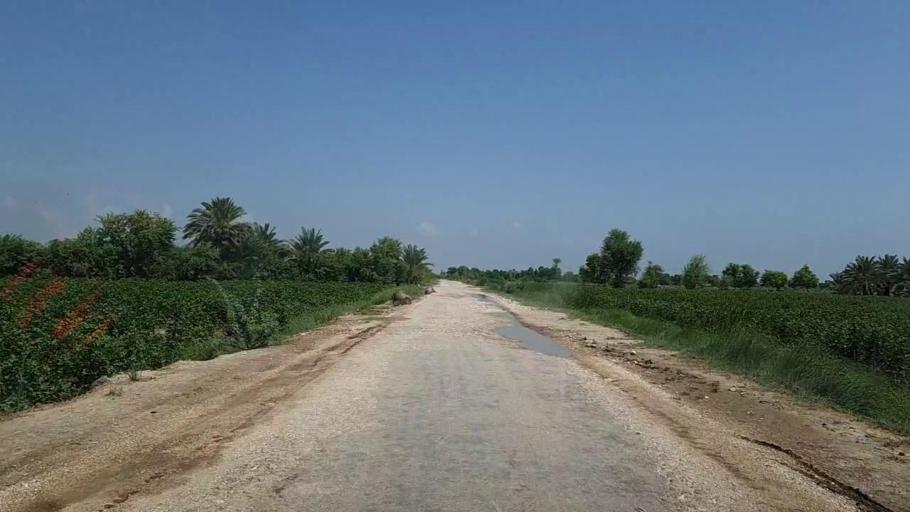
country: PK
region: Sindh
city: Bhiria
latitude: 26.8979
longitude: 68.2178
